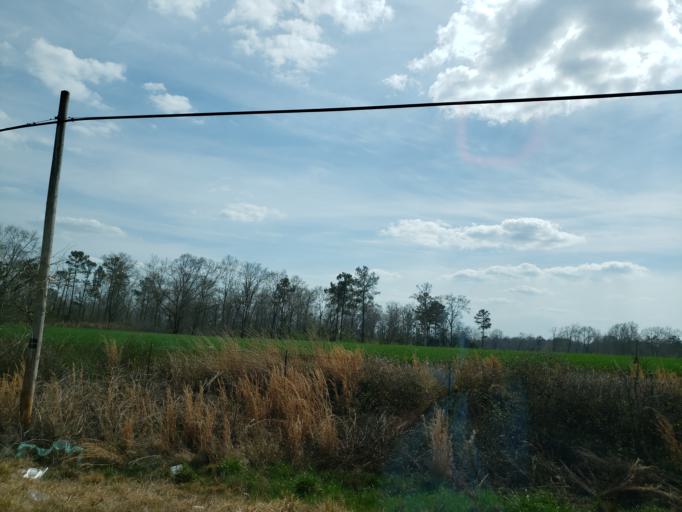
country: US
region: Alabama
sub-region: Macon County
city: Tuskegee
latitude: 32.5818
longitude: -85.7282
